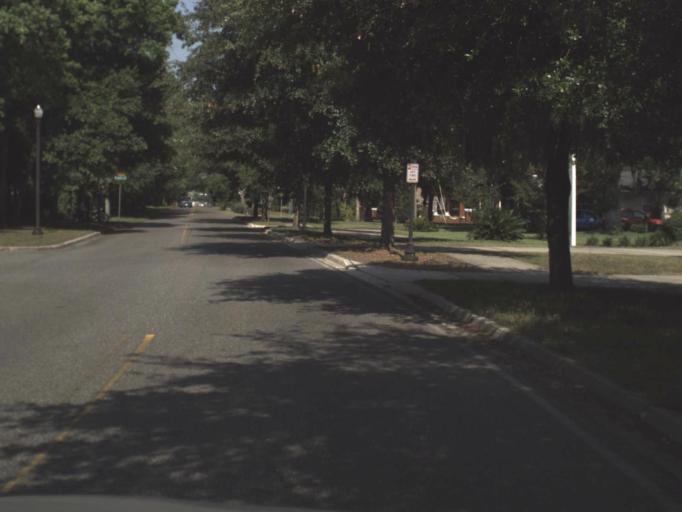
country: US
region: Florida
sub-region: Duval County
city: Jacksonville
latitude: 30.2822
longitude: -81.7086
